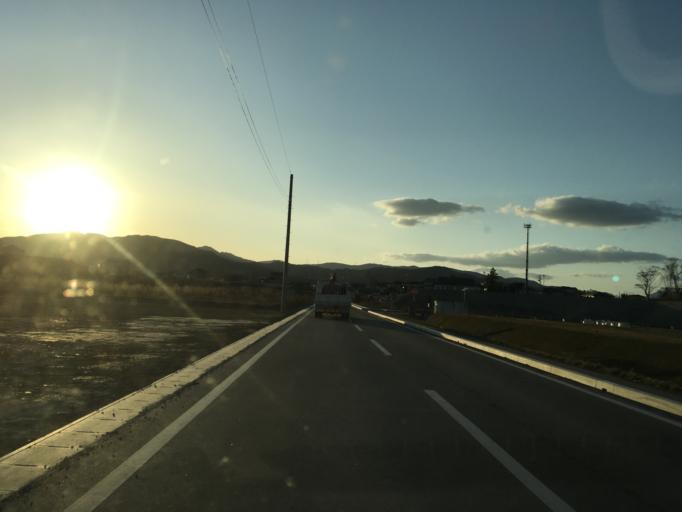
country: JP
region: Iwate
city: Ofunato
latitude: 38.8298
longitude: 141.5912
